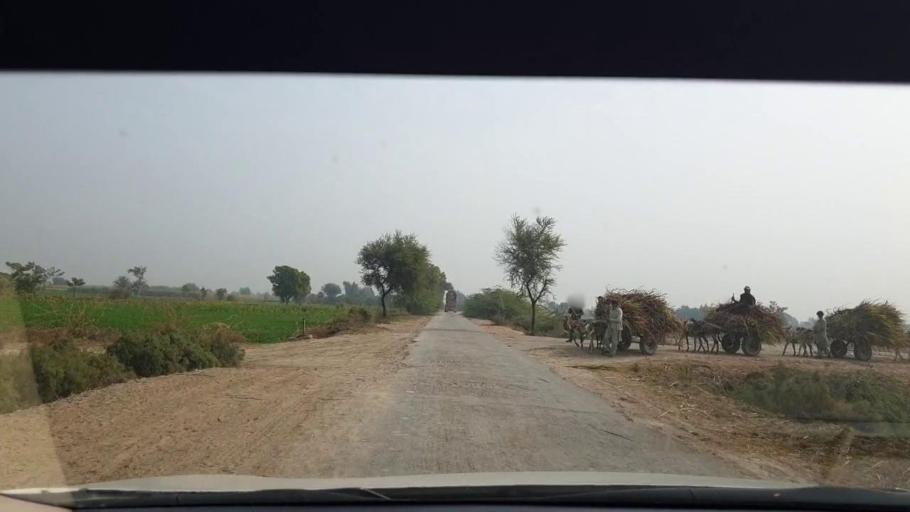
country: PK
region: Sindh
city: Berani
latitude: 25.8473
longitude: 68.8267
